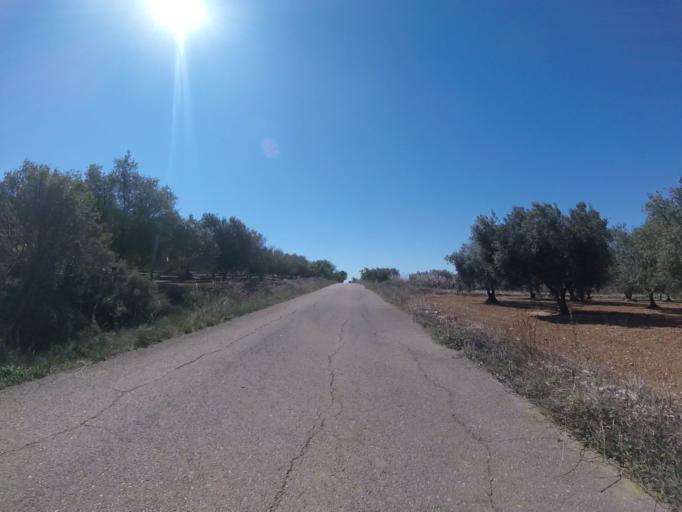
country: ES
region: Valencia
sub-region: Provincia de Castello
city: Cuevas de Vinroma
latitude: 40.3878
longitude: 0.1592
